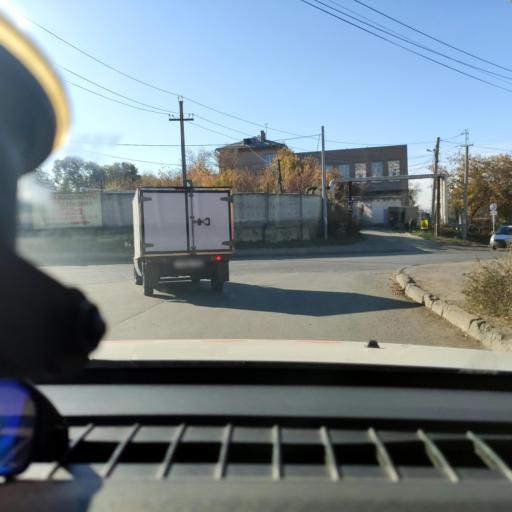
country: RU
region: Samara
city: Samara
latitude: 53.1858
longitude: 50.1463
